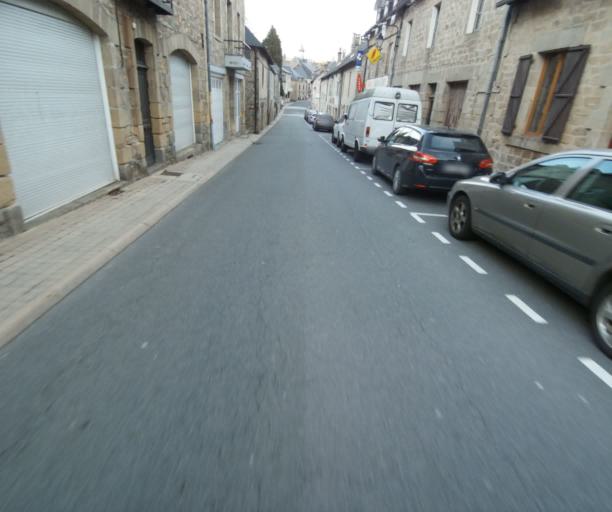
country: FR
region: Limousin
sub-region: Departement de la Correze
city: Correze
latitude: 45.3701
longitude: 1.8734
